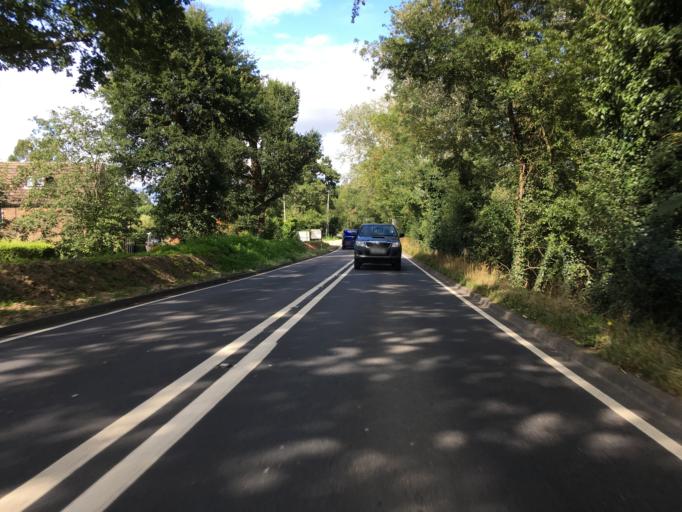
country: GB
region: England
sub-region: West Sussex
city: Southwater
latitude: 51.0593
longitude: -0.3826
